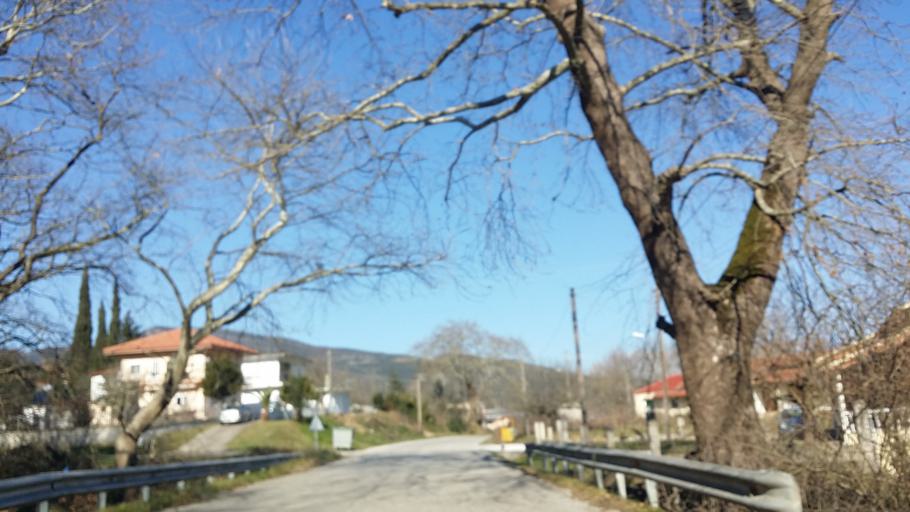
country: GR
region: West Greece
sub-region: Nomos Aitolias kai Akarnanias
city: Sardinia
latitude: 38.8632
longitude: 21.3378
